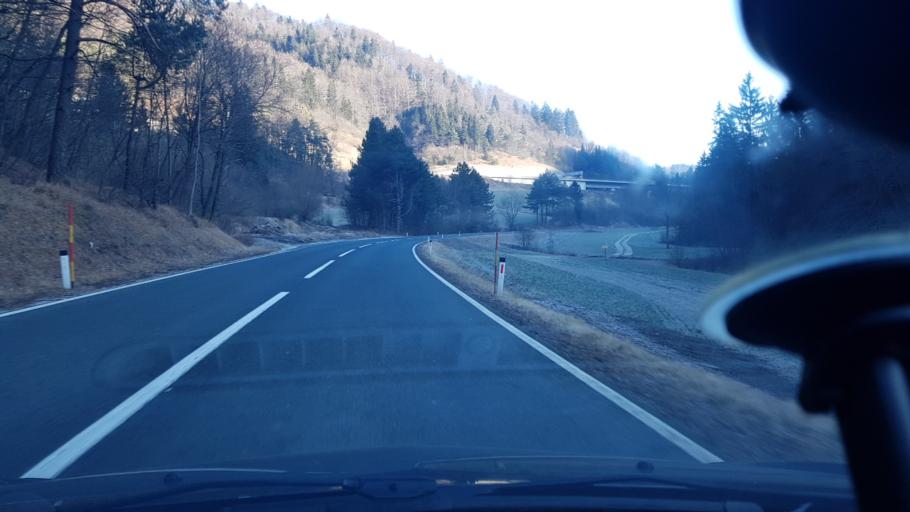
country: SI
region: Zagorje ob Savi
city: Izlake
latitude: 46.1785
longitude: 14.8463
